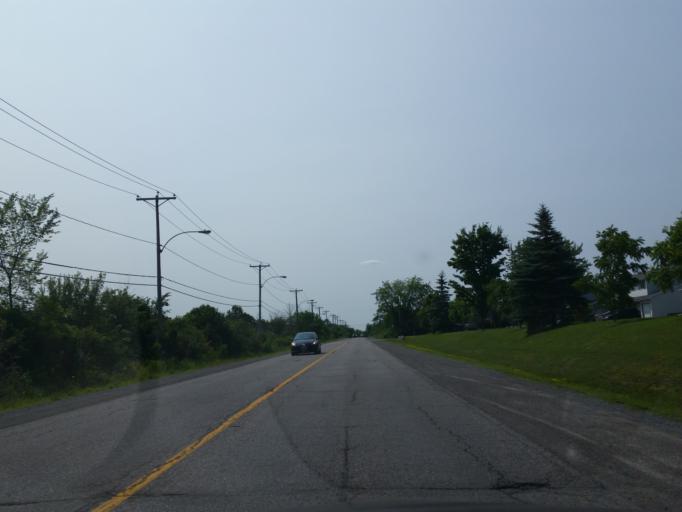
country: CA
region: Ontario
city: Bells Corners
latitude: 45.3853
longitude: -75.8253
